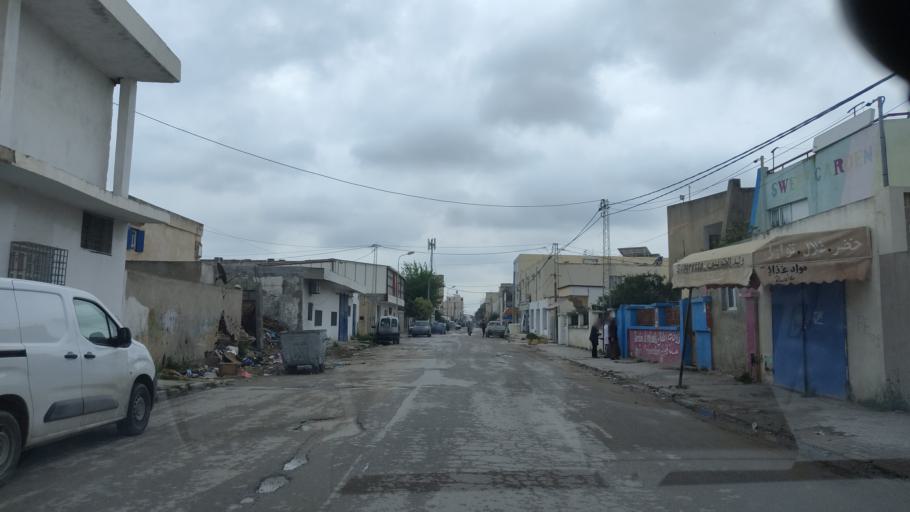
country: TN
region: Ariana
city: Ariana
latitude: 36.8759
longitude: 10.2179
